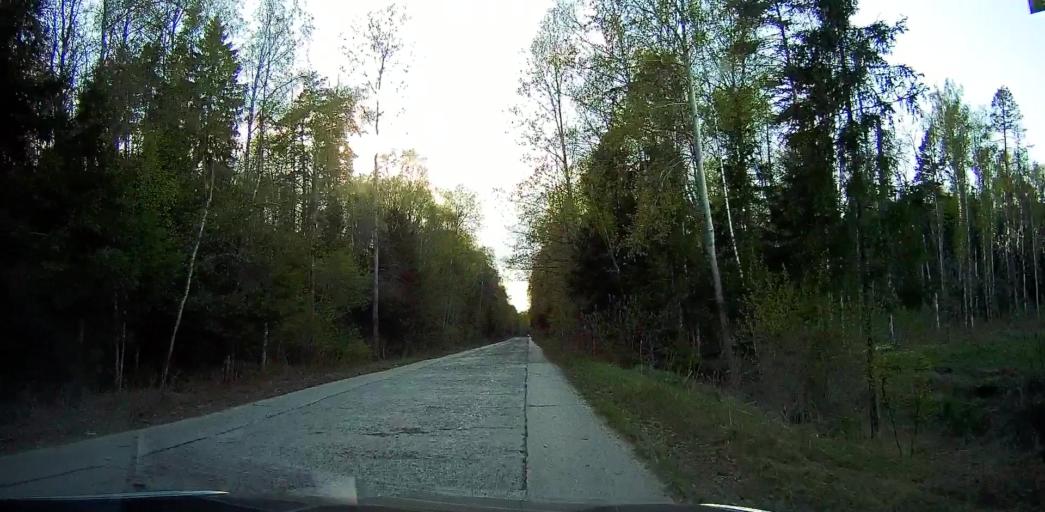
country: RU
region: Moskovskaya
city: Malyshevo
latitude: 55.5337
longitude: 38.3960
